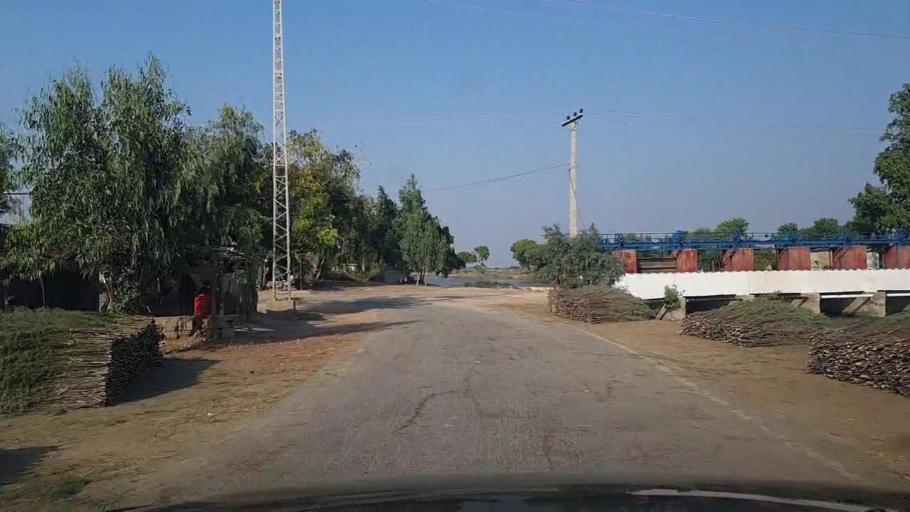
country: PK
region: Sindh
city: Thatta
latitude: 24.6157
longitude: 68.0515
